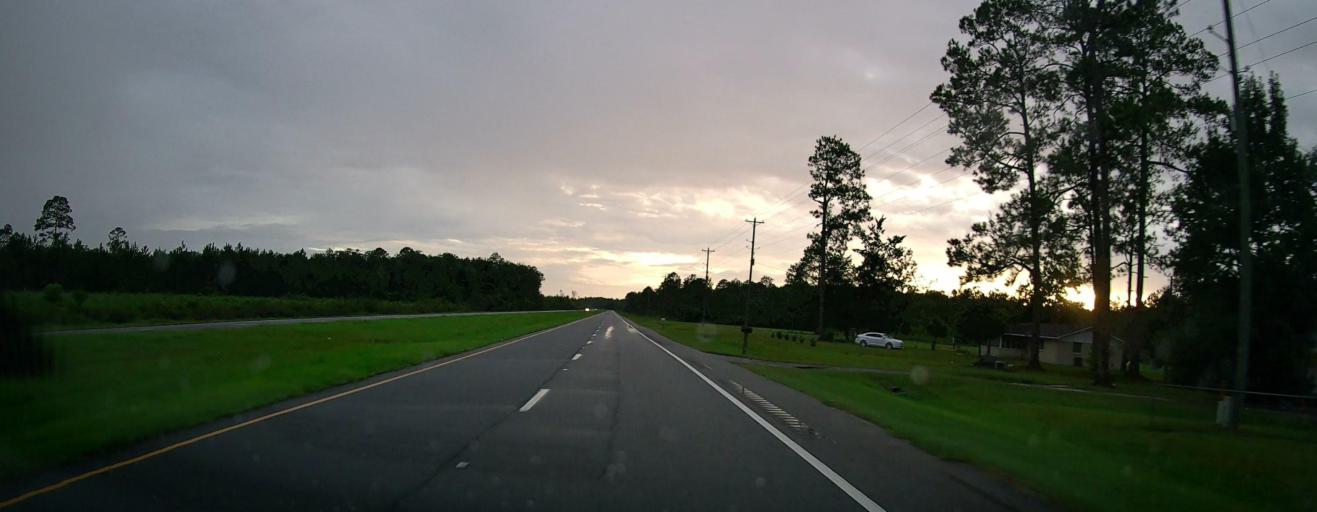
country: US
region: Georgia
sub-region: Clinch County
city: Homerville
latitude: 31.0136
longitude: -82.8363
